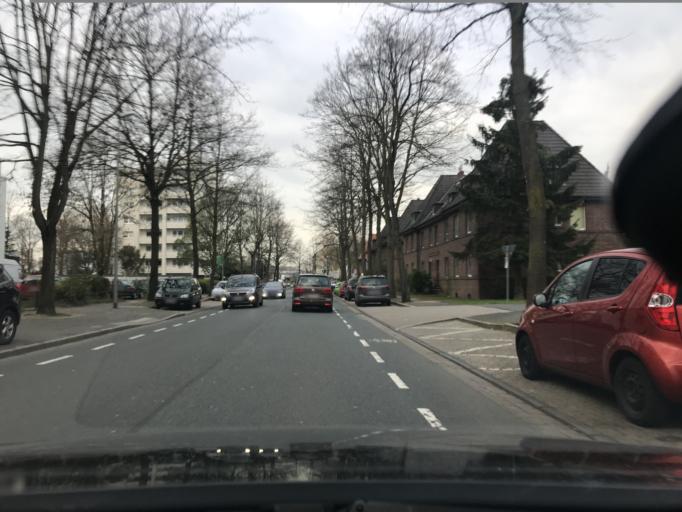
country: DE
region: North Rhine-Westphalia
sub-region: Regierungsbezirk Dusseldorf
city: Wesel
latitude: 51.6621
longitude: 6.6258
